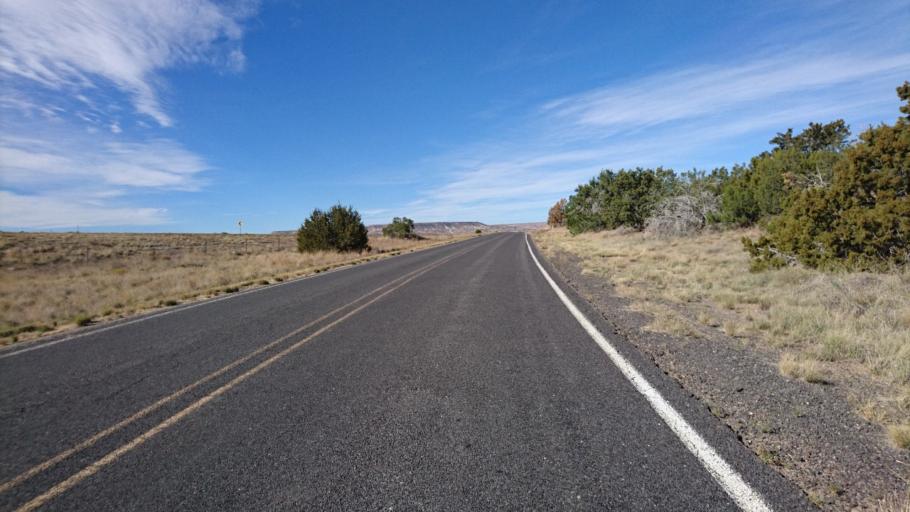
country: US
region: New Mexico
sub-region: Cibola County
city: Laguna
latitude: 35.0399
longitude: -107.3628
